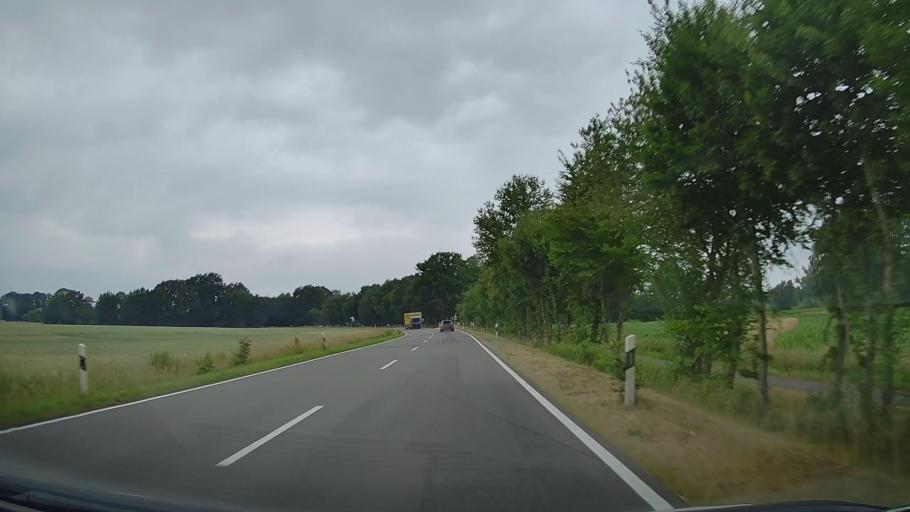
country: DE
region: Lower Saxony
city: Dinklage
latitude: 52.6798
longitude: 8.0882
